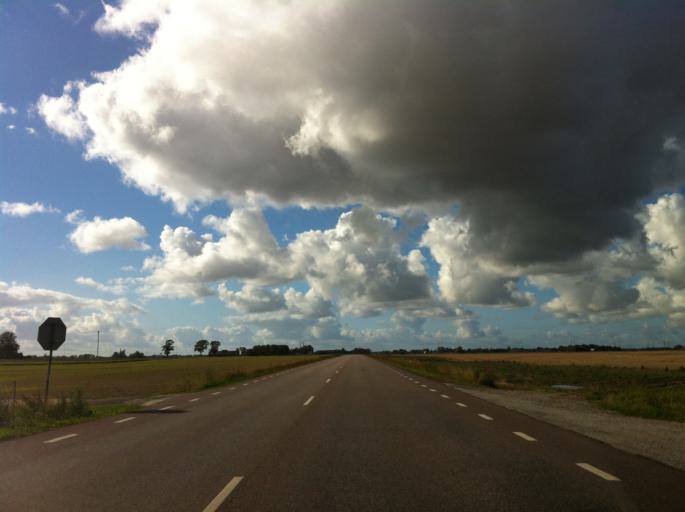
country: SE
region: Skane
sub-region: Lunds Kommun
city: Lund
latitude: 55.7921
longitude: 13.2164
